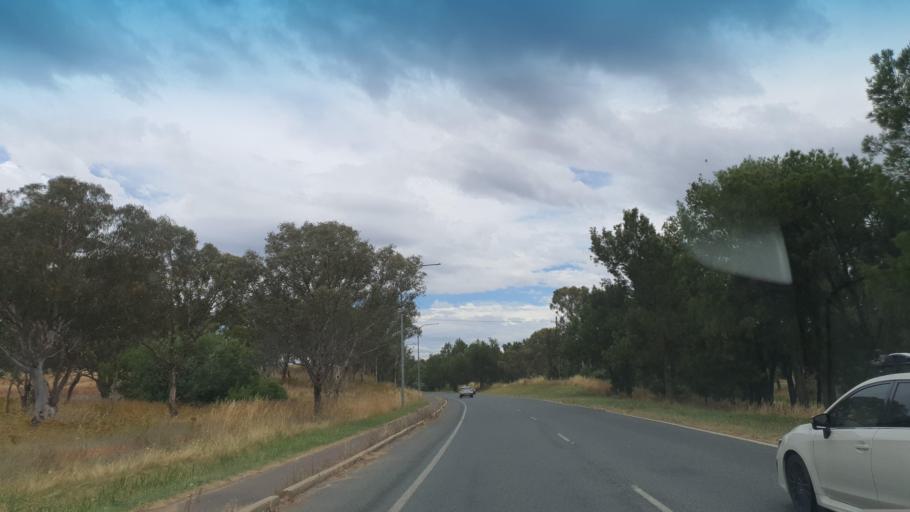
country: AU
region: Australian Capital Territory
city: Belconnen
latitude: -35.2114
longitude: 149.0382
